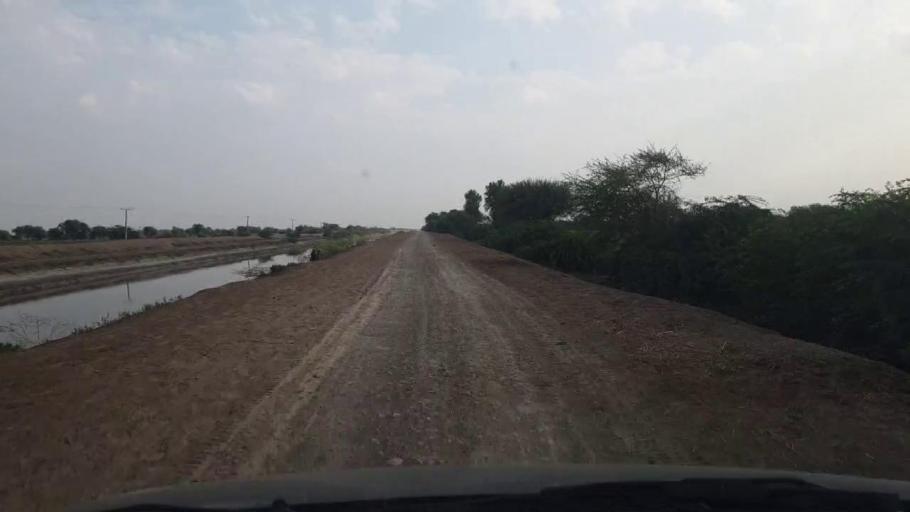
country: PK
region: Sindh
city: Badin
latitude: 24.5213
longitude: 68.6821
